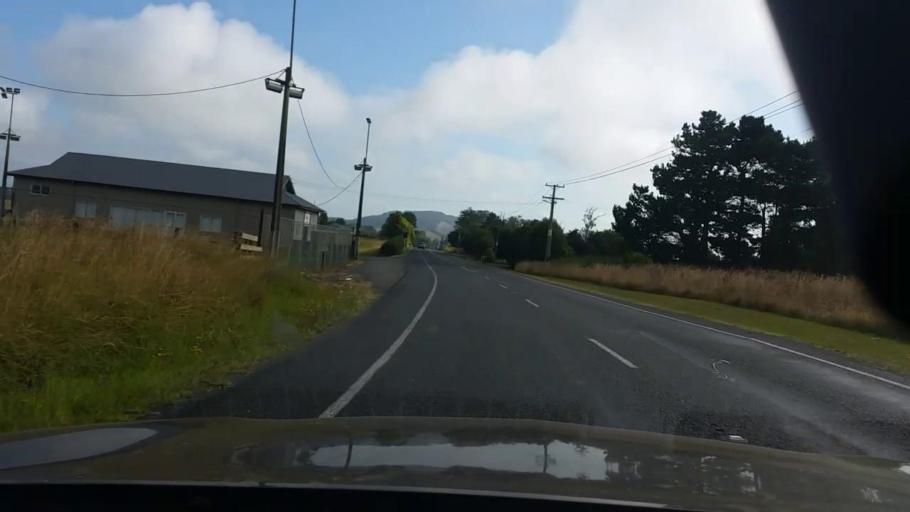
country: NZ
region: Waikato
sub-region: Hamilton City
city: Hamilton
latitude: -37.6142
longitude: 175.3445
